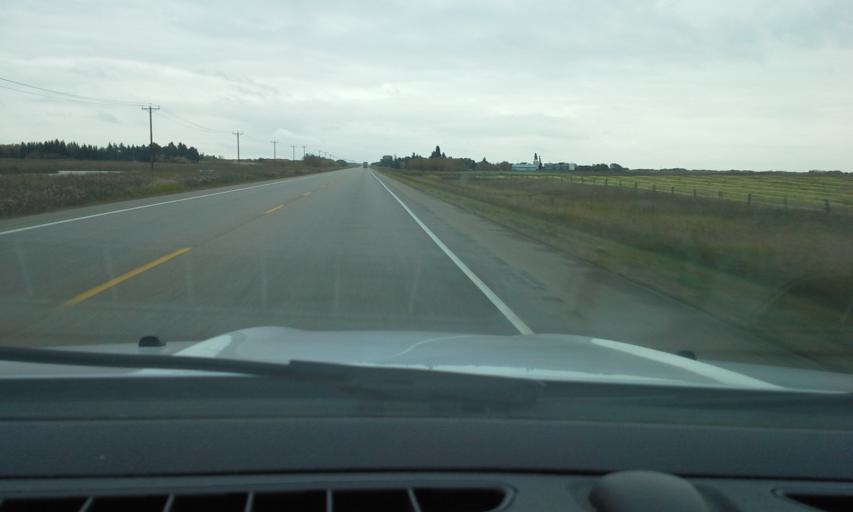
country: CA
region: Saskatchewan
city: Lloydminster
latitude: 53.2780
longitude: -109.8646
